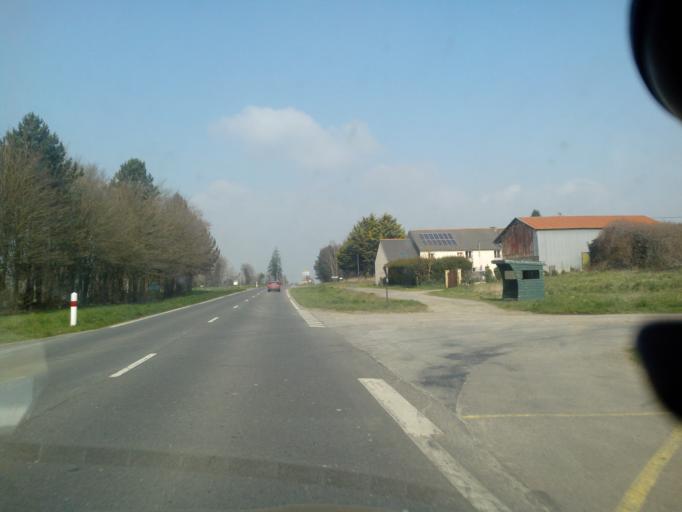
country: FR
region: Brittany
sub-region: Departement d'Ille-et-Vilaine
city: Quedillac
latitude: 48.2303
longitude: -2.1754
